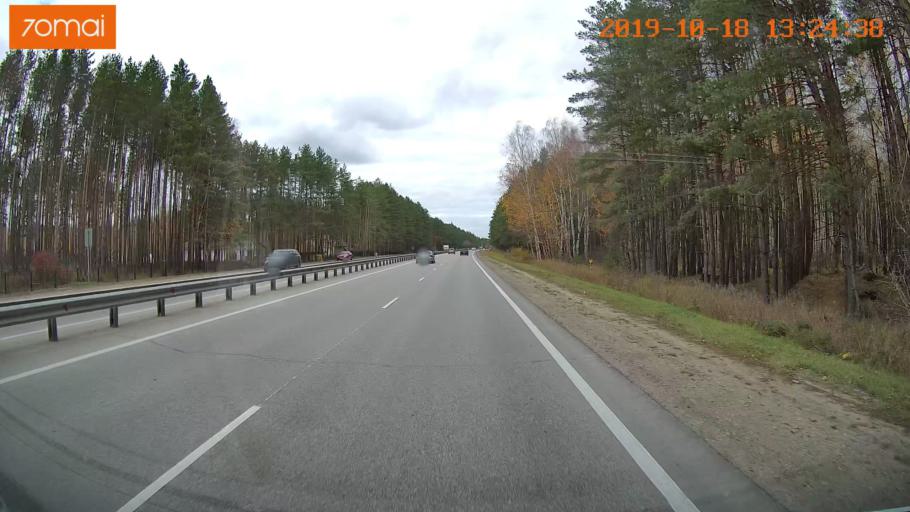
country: RU
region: Rjazan
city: Polyany
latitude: 54.7335
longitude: 39.8427
